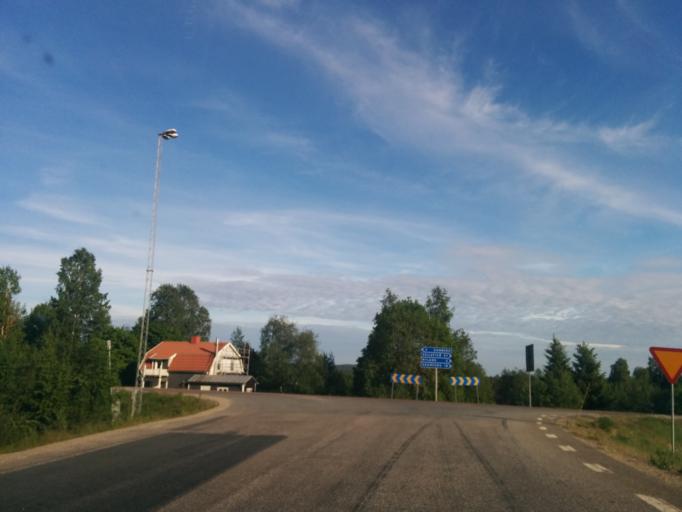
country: SE
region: Vaesternorrland
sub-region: Kramfors Kommun
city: Kramfors
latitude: 63.0233
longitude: 17.7639
